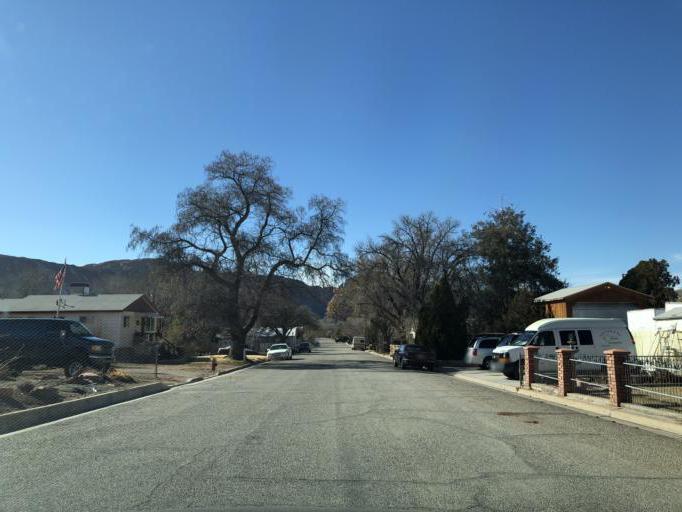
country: US
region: Utah
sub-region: Grand County
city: Moab
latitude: 38.5701
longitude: -109.5397
